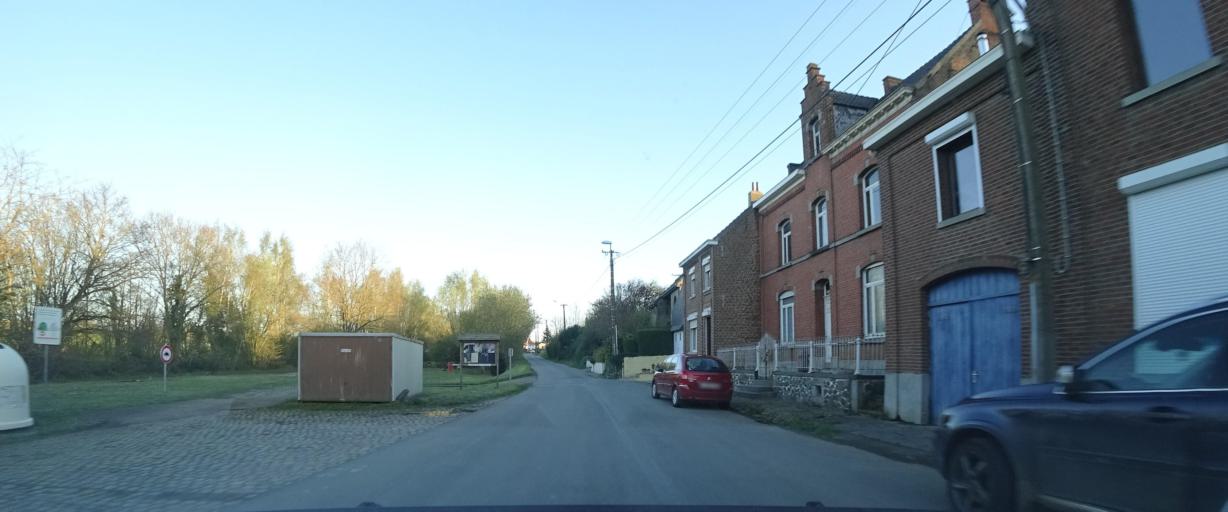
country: BE
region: Wallonia
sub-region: Province du Brabant Wallon
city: Rebecq-Rognon
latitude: 50.6520
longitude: 4.1063
